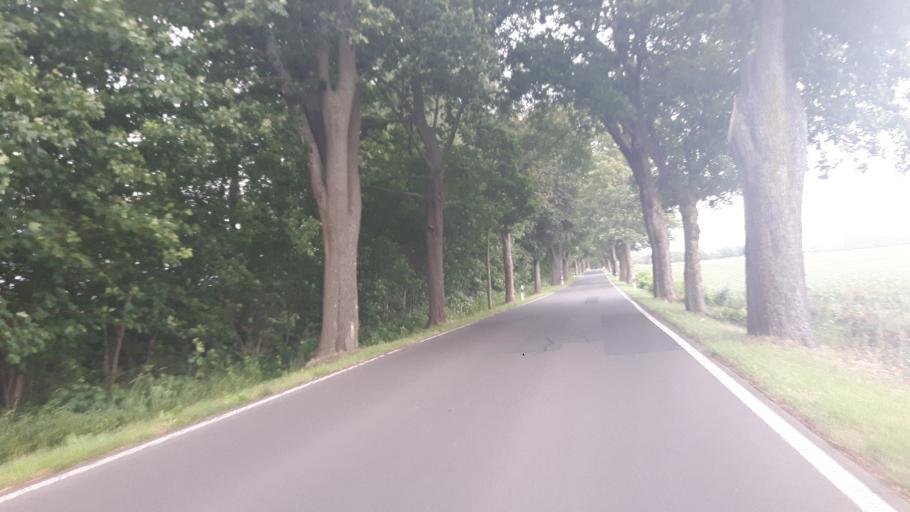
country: DE
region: Brandenburg
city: Eberswalde
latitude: 52.7728
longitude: 13.8492
